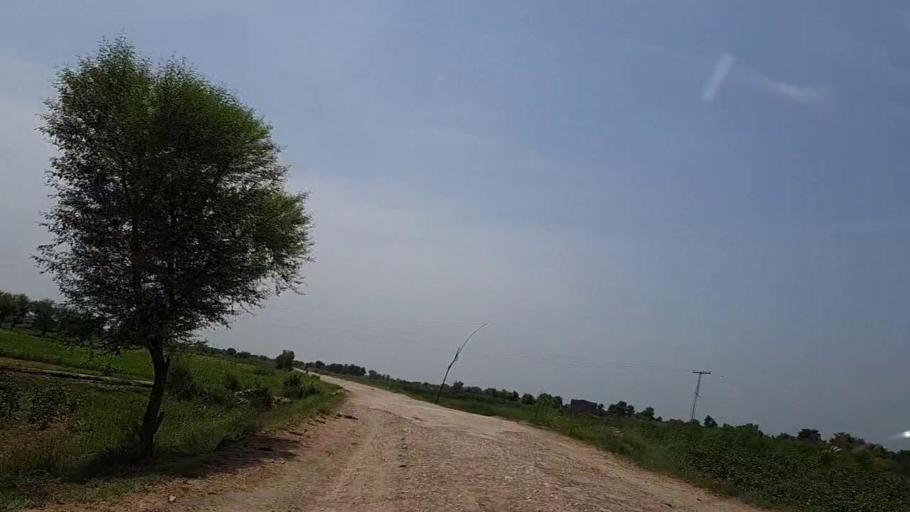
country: PK
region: Sindh
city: Khanpur
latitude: 27.8640
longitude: 69.4874
